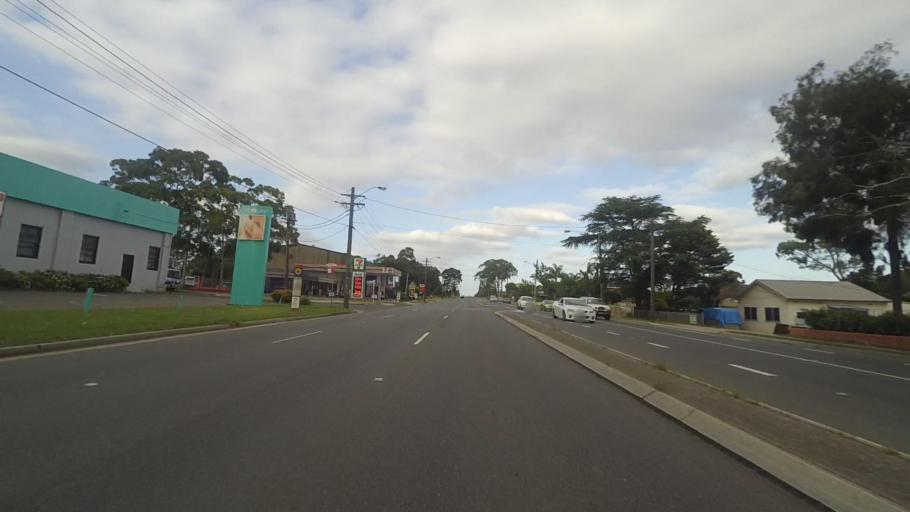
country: AU
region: New South Wales
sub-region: Bankstown
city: Revesby
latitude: -33.9375
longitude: 151.0205
